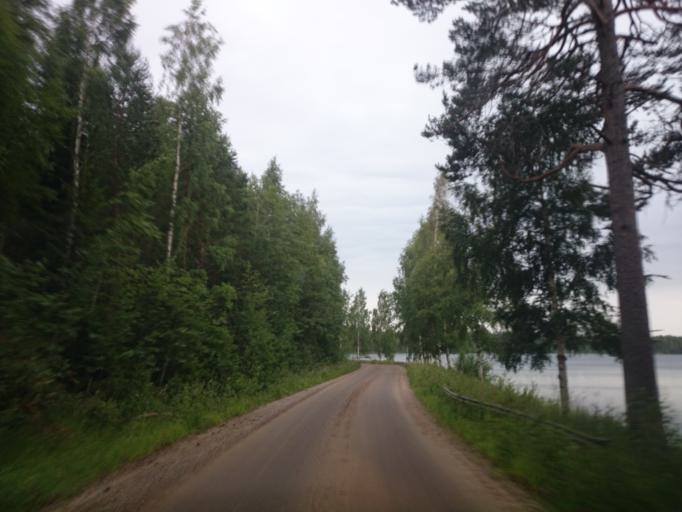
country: SE
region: Vaesternorrland
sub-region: Sundsvalls Kommun
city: Njurundabommen
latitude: 62.1355
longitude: 17.4149
